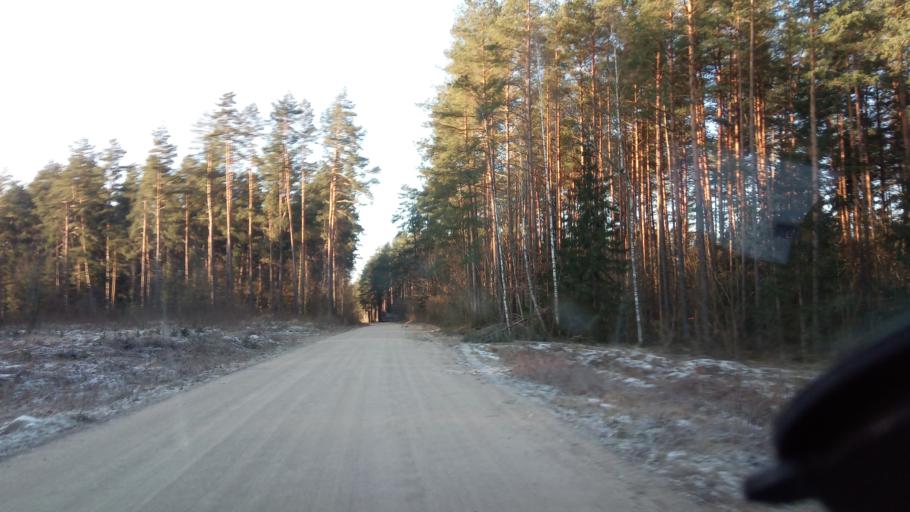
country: LT
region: Alytaus apskritis
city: Druskininkai
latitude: 54.1538
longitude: 23.9406
